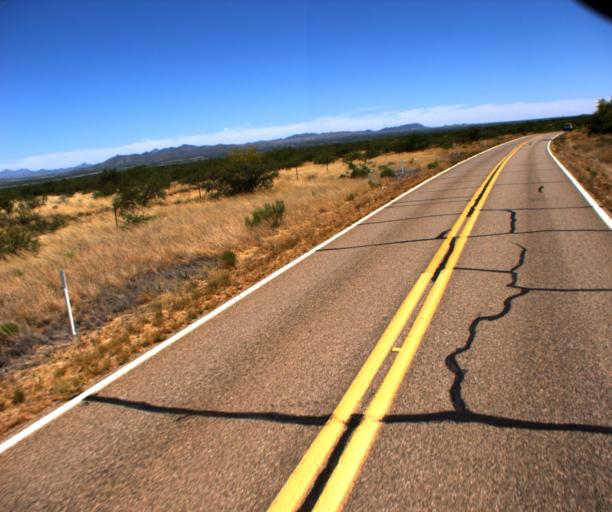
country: US
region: Arizona
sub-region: Pima County
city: Three Points
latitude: 31.6932
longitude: -111.4871
